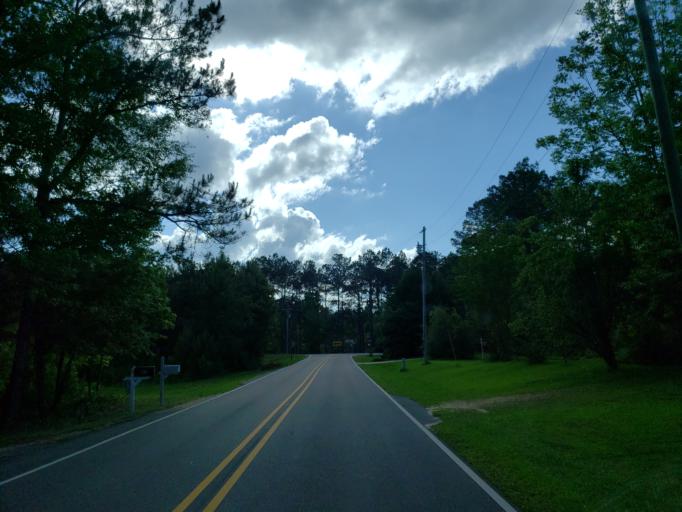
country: US
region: Mississippi
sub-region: Lamar County
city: Sumrall
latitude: 31.3551
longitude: -89.4975
